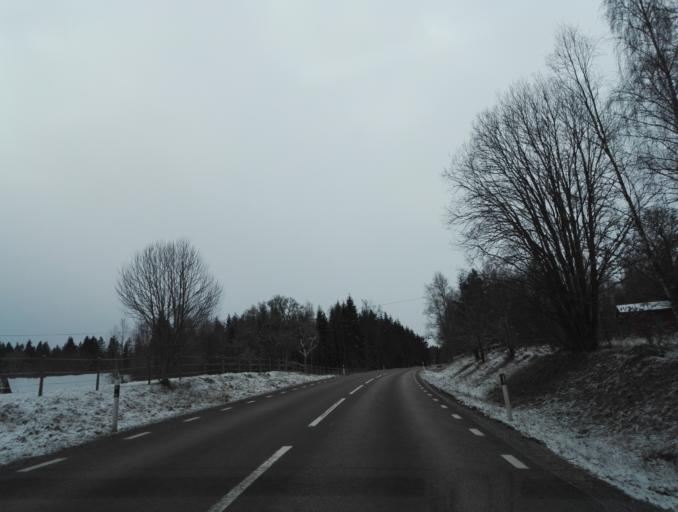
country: SE
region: Kalmar
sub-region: Hultsfreds Kommun
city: Virserum
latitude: 57.1962
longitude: 15.5110
